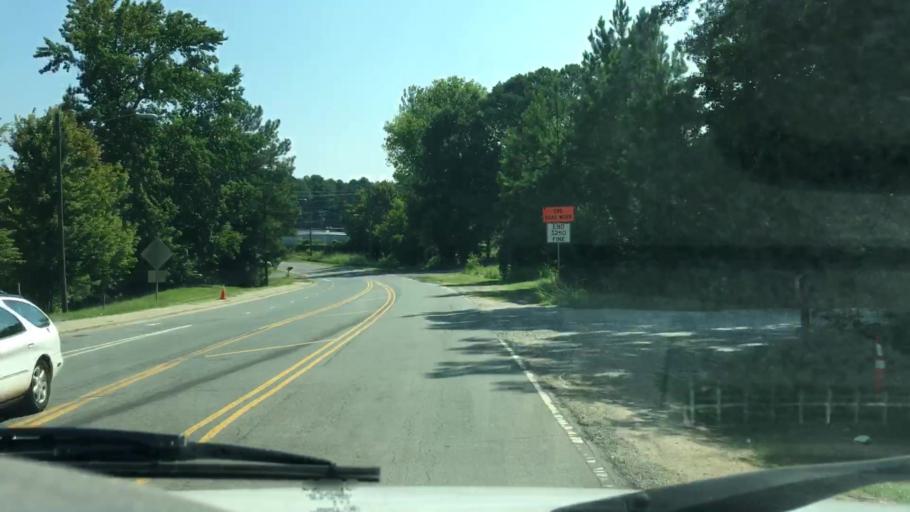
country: US
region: North Carolina
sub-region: Mecklenburg County
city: Huntersville
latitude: 35.3342
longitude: -80.8464
